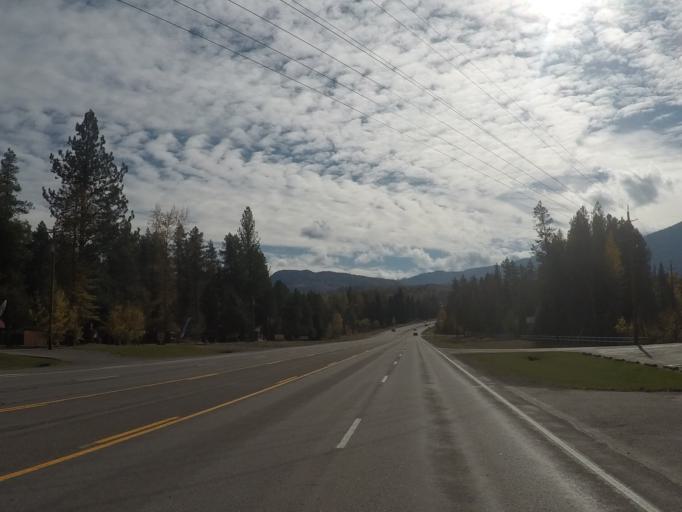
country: US
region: Montana
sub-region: Flathead County
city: Columbia Falls
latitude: 48.4005
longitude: -114.0425
